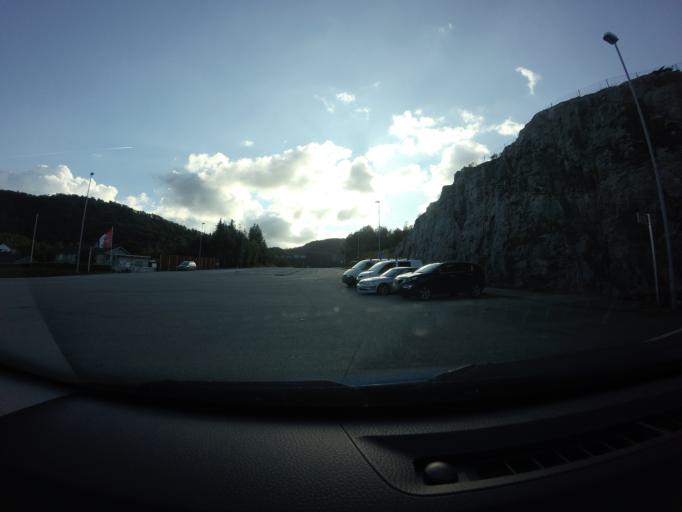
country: NO
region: Rogaland
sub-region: Forsand
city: Forsand
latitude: 58.8947
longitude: 6.0546
